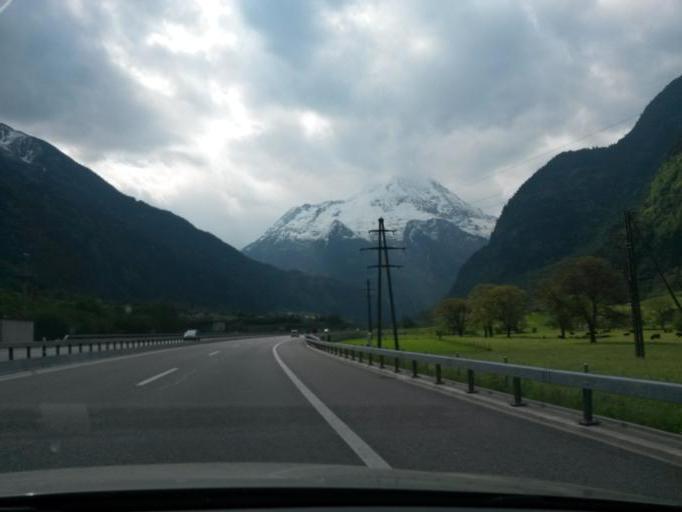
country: CH
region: Uri
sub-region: Uri
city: Erstfeld
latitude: 46.8105
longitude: 8.6588
